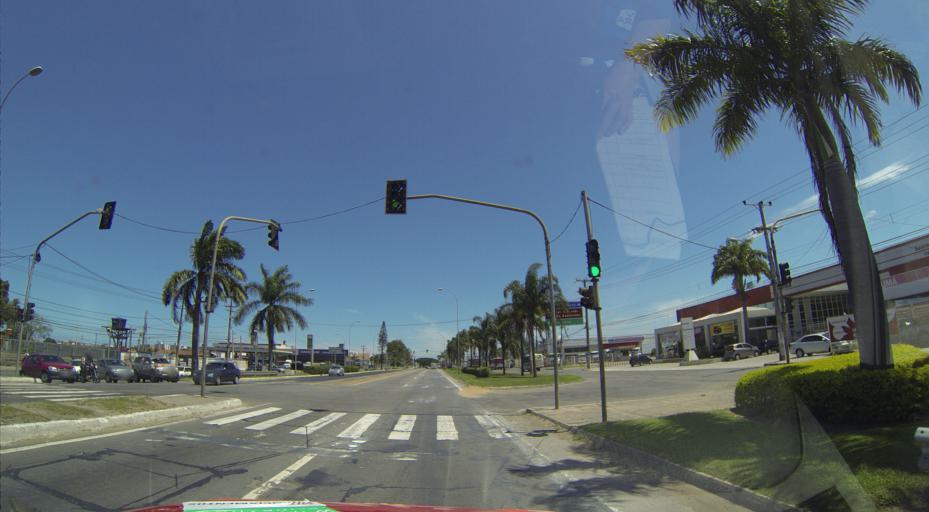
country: BR
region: Espirito Santo
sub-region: Serra
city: Serra
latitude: -20.2061
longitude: -40.2694
